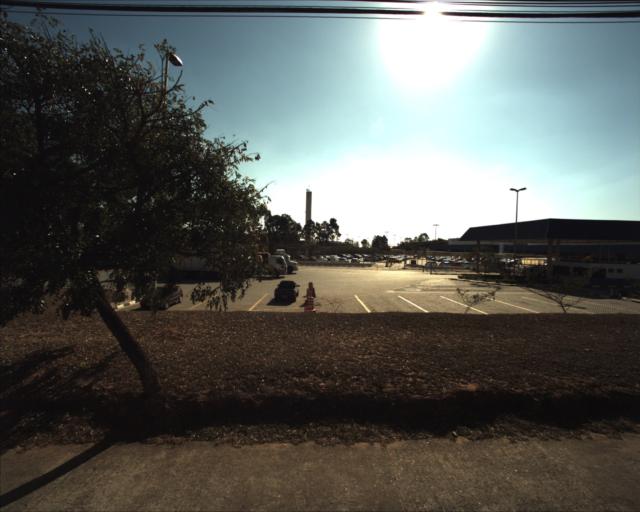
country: BR
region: Sao Paulo
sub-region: Sorocaba
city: Sorocaba
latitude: -23.4586
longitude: -47.4207
